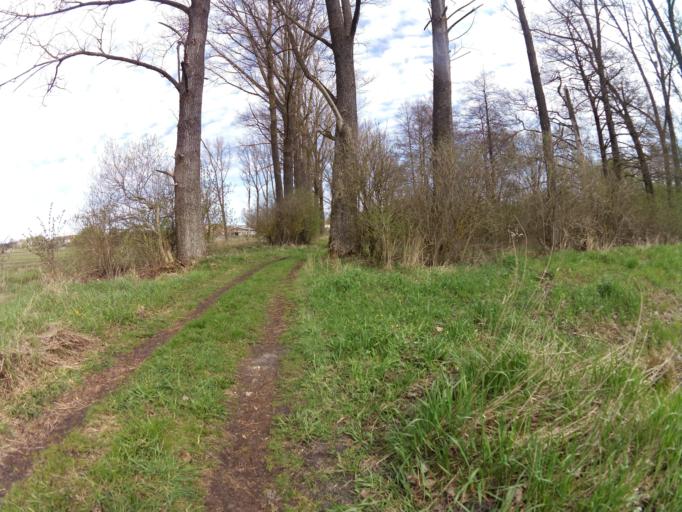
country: PL
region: West Pomeranian Voivodeship
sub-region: Powiat szczecinecki
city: Borne Sulinowo
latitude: 53.7053
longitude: 16.5389
